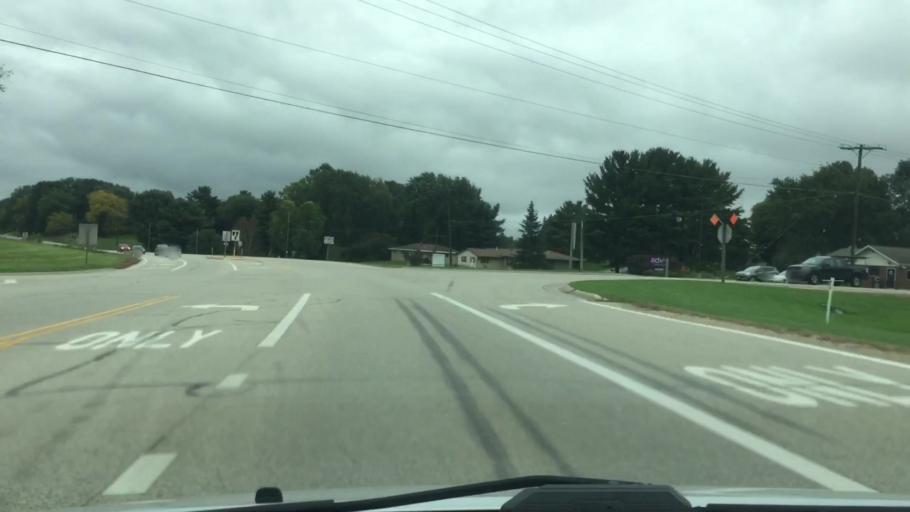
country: US
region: Wisconsin
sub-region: Walworth County
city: Elkhorn
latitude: 42.7419
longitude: -88.5530
